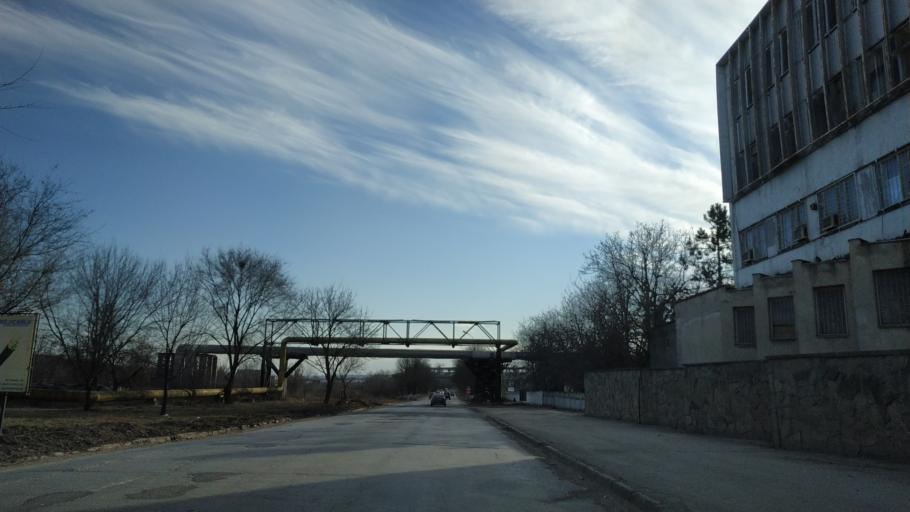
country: MD
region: Chisinau
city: Chisinau
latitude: 47.0315
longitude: 28.8967
